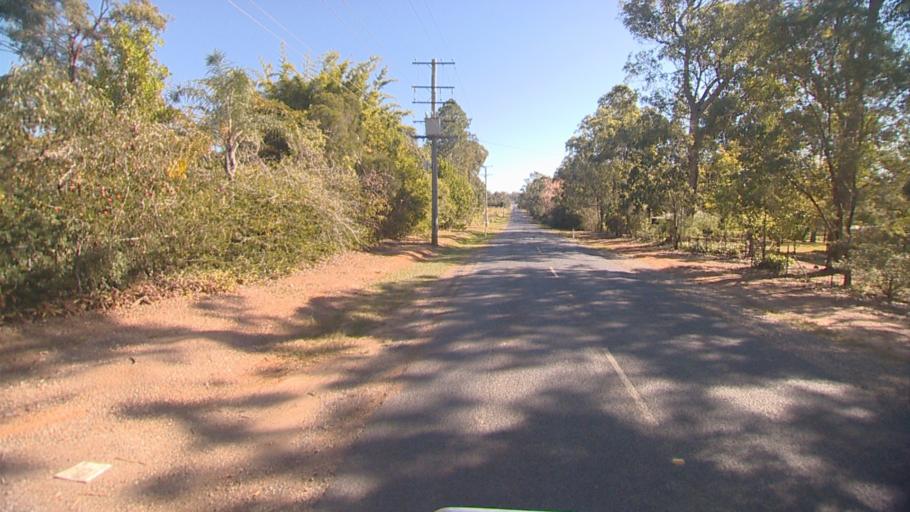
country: AU
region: Queensland
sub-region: Logan
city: Logan Reserve
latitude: -27.7122
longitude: 153.1025
